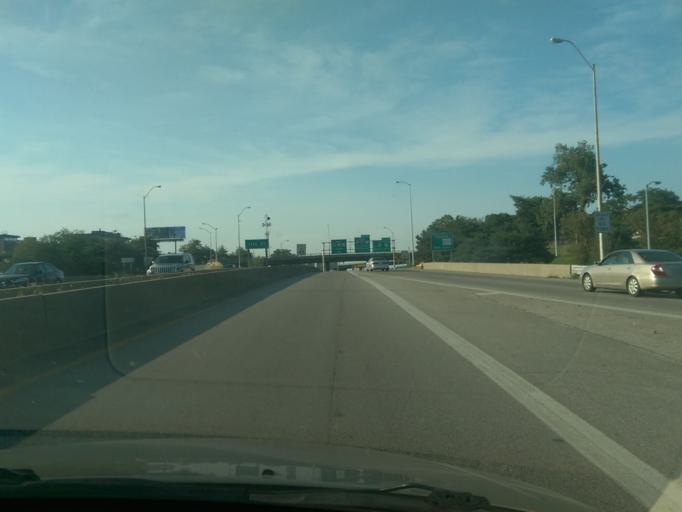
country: US
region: Missouri
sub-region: Jackson County
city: Kansas City
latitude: 39.1002
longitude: -94.5726
